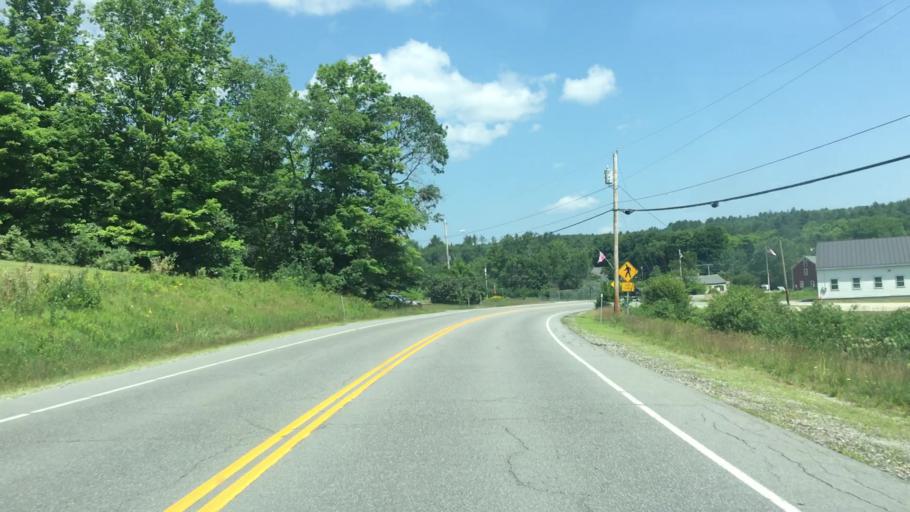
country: US
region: New Hampshire
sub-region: Sullivan County
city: Grantham
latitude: 43.4496
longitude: -72.1620
